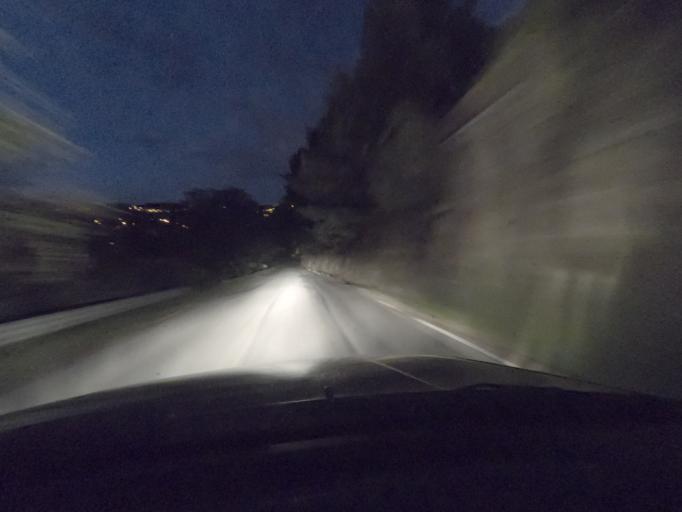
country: PT
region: Vila Real
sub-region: Mesao Frio
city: Mesao Frio
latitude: 41.1947
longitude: -7.8481
